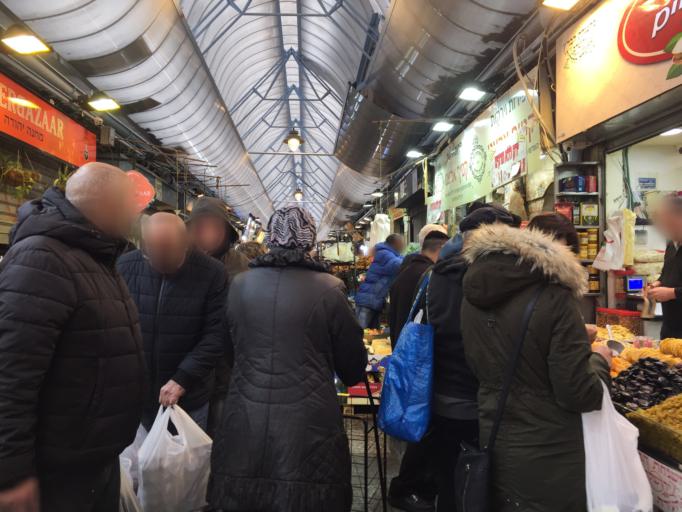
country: IL
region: Jerusalem
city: West Jerusalem
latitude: 31.7856
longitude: 35.2128
